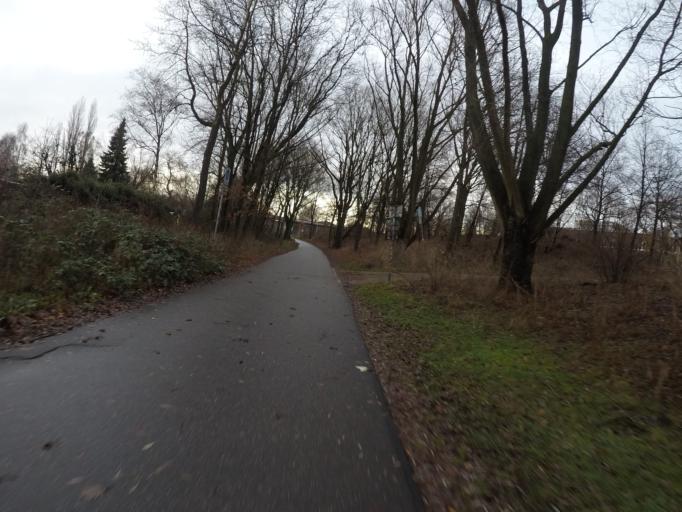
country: DE
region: Hamburg
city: Kleiner Grasbrook
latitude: 53.5187
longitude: 10.0145
